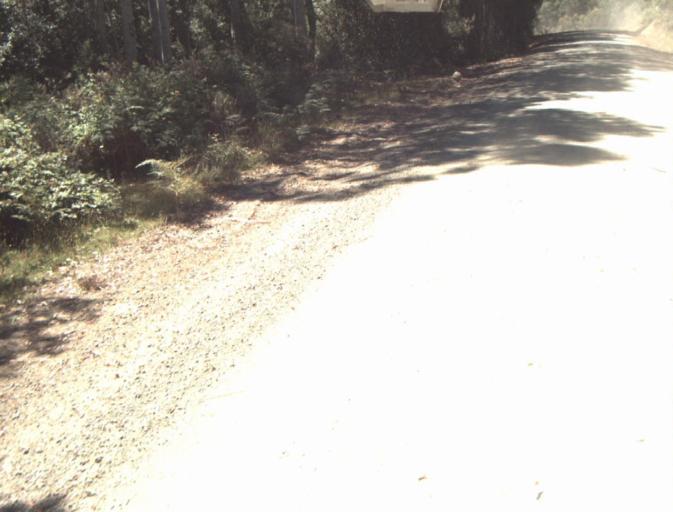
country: AU
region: Tasmania
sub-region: Dorset
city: Scottsdale
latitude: -41.3372
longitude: 147.4333
